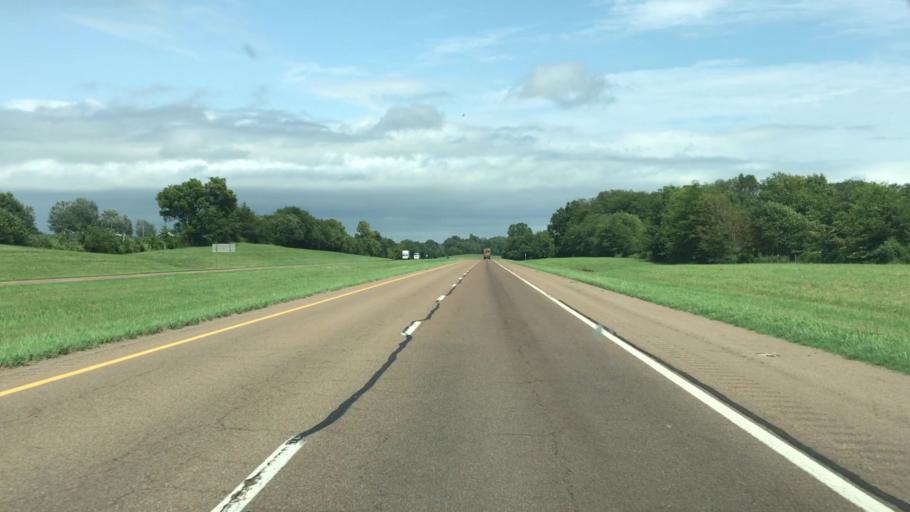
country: US
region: Tennessee
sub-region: Obion County
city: South Fulton
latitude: 36.4907
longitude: -88.9225
